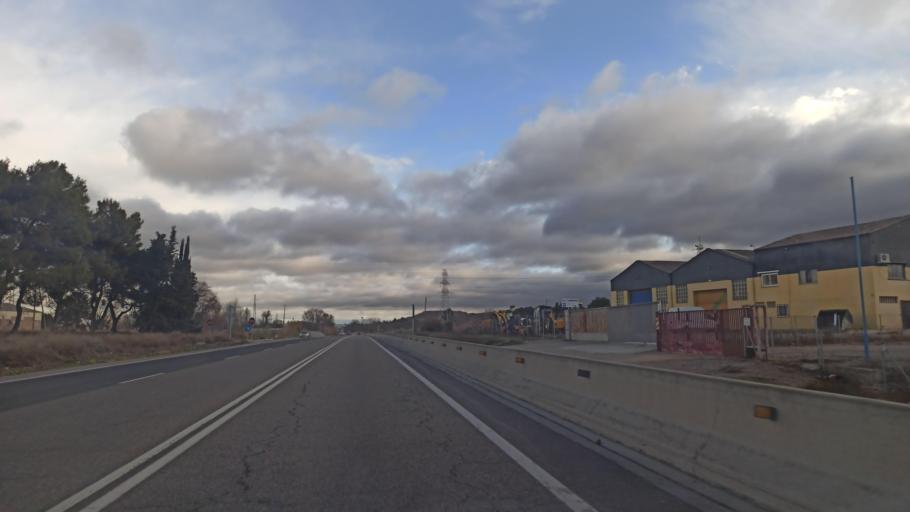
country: ES
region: Catalonia
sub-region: Provincia de Lleida
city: Alcoletge
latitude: 41.6326
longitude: 0.6665
